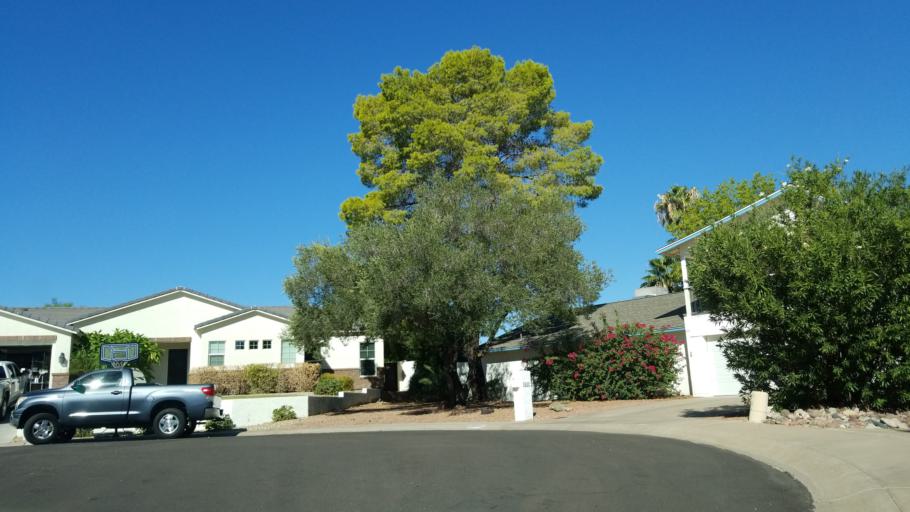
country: US
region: Arizona
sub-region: Maricopa County
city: Paradise Valley
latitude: 33.5920
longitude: -112.0333
